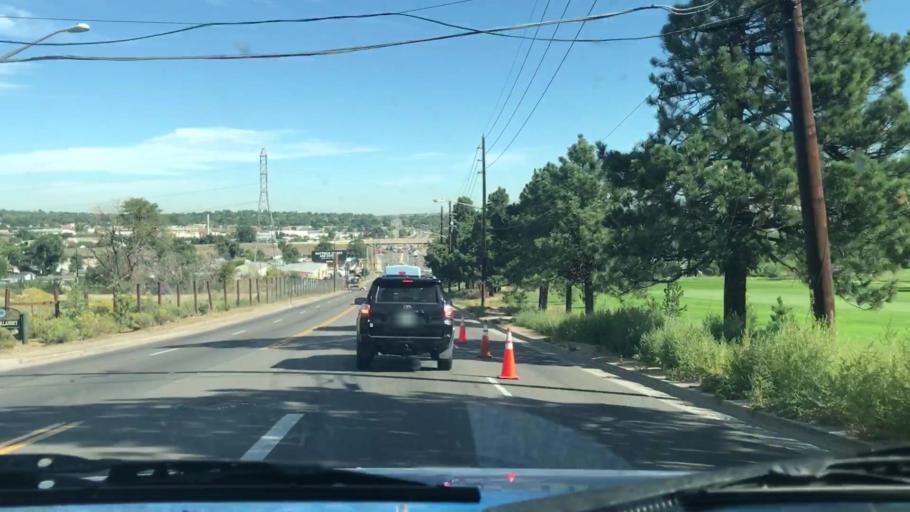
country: US
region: Colorado
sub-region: Adams County
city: Berkley
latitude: 39.7891
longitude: -105.0533
